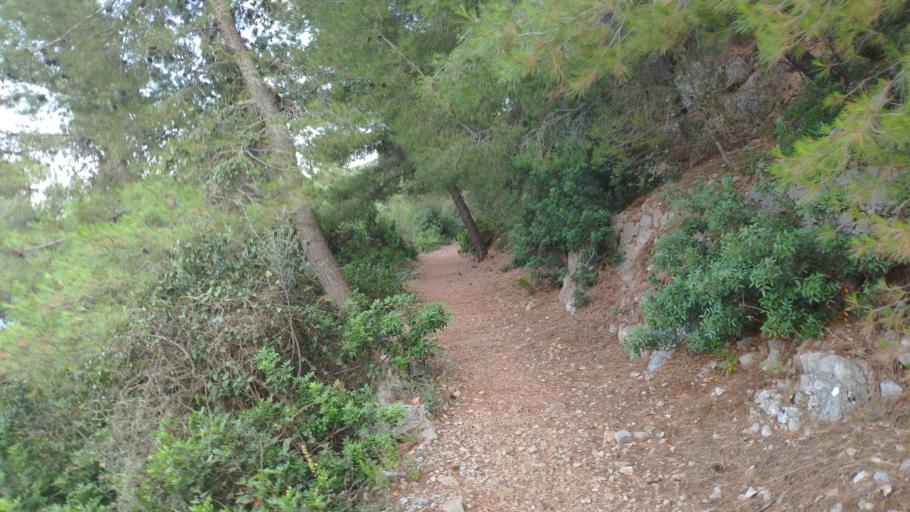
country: GR
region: Peloponnese
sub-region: Nomos Lakonias
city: Sykea
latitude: 36.9707
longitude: 22.9960
